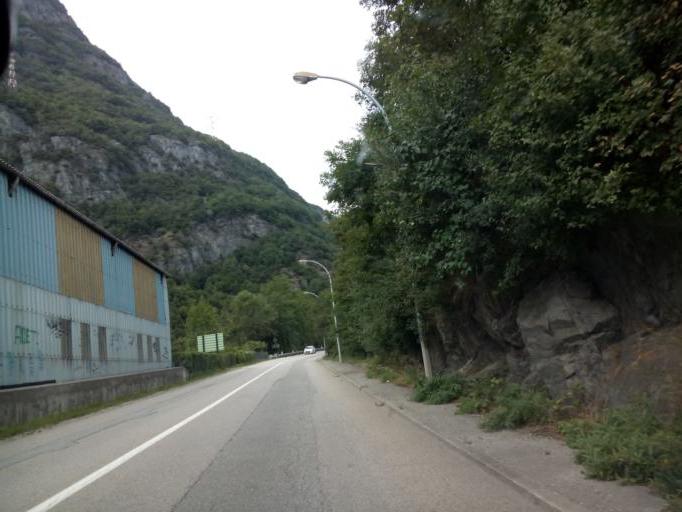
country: FR
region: Rhone-Alpes
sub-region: Departement de l'Isere
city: Vaulnaveys-le-Bas
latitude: 45.0745
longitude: 5.8775
